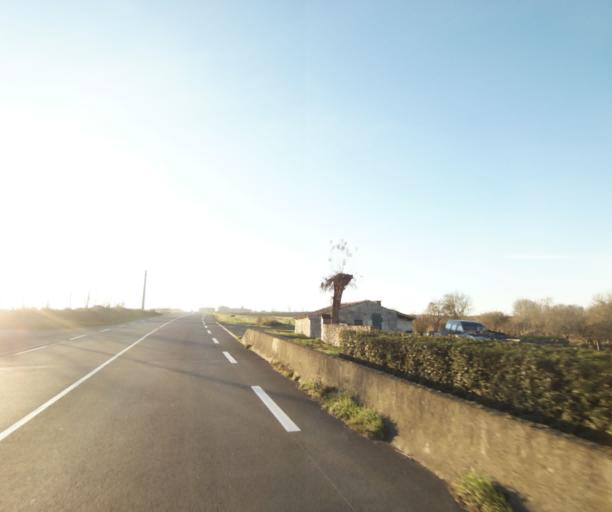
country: FR
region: Poitou-Charentes
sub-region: Departement de la Charente-Maritime
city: Cherac
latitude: 45.7174
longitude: -0.4944
